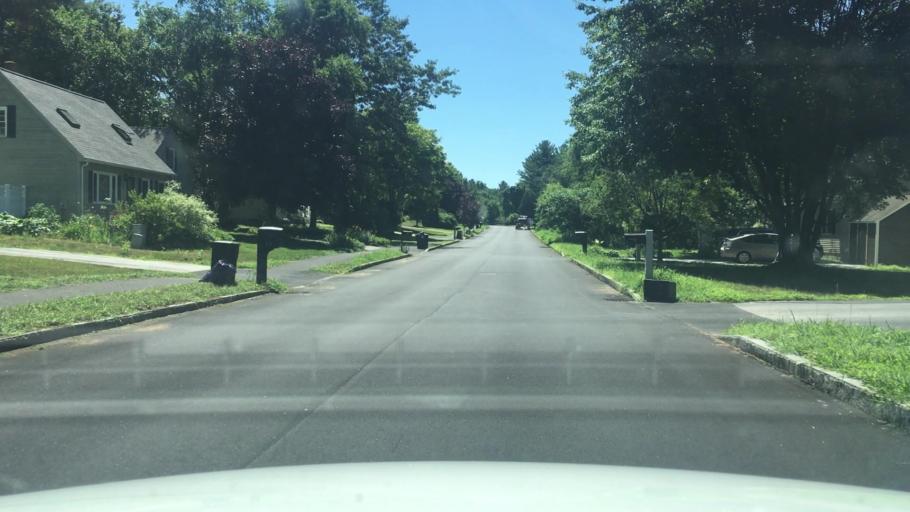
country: US
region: New Hampshire
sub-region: Merrimack County
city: Boscawen
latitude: 43.2747
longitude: -71.6028
